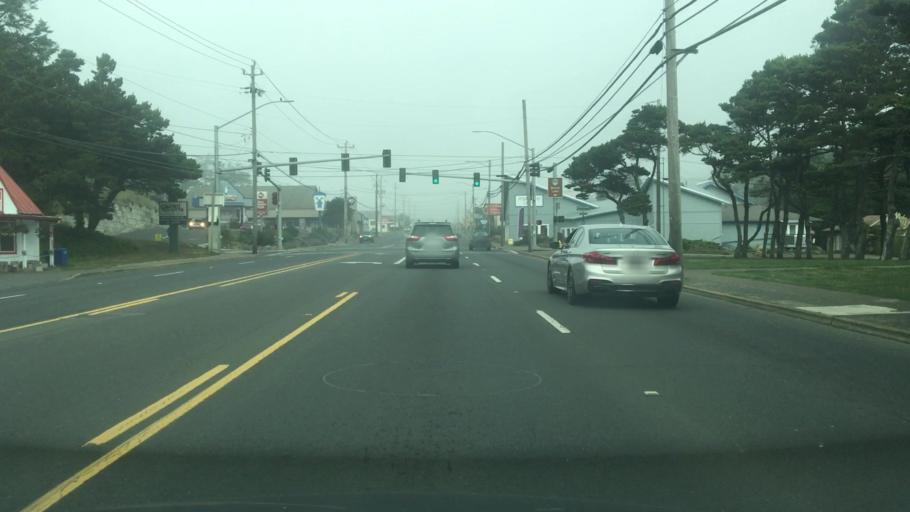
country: US
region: Oregon
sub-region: Lincoln County
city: Lincoln City
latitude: 44.9704
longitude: -124.0148
